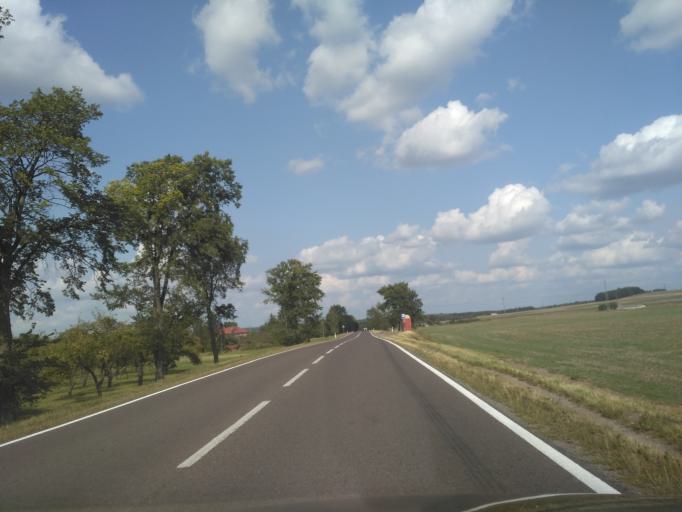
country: PL
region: Lublin Voivodeship
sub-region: Powiat chelmski
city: Rejowiec
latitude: 51.1119
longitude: 23.3203
